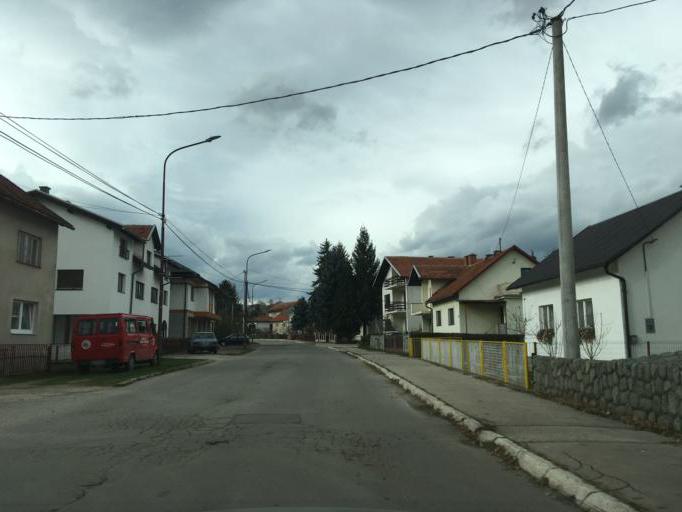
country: BA
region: Federation of Bosnia and Herzegovina
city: Bugojno
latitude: 44.0534
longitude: 17.4423
